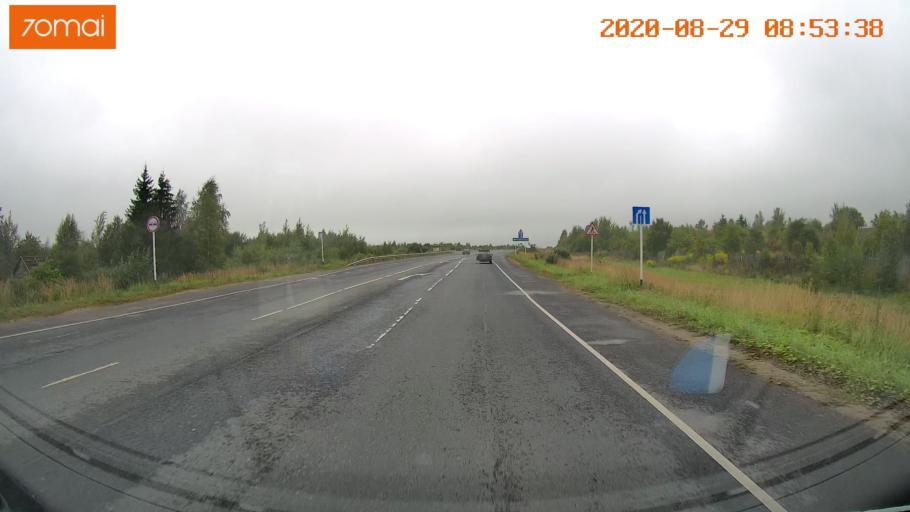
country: RU
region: Ivanovo
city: Staraya Vichuga
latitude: 57.2246
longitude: 41.8628
